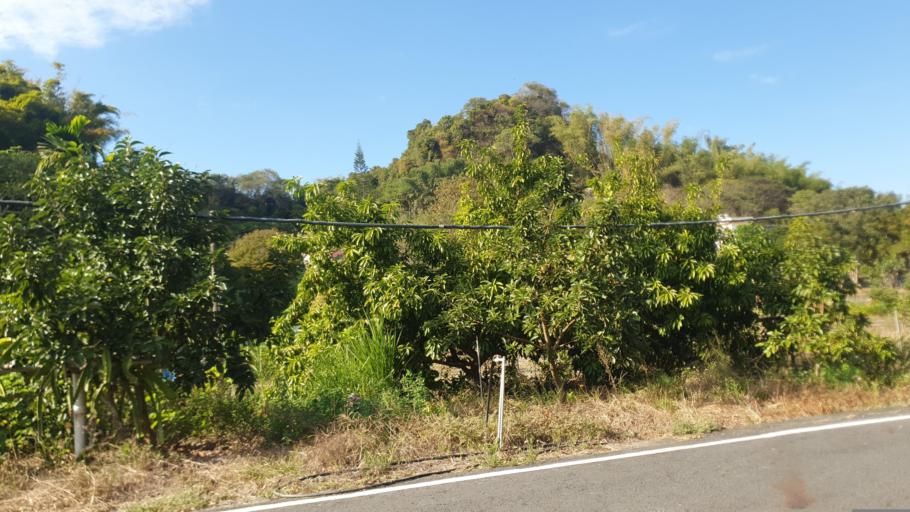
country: TW
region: Taiwan
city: Yujing
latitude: 23.0187
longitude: 120.3973
